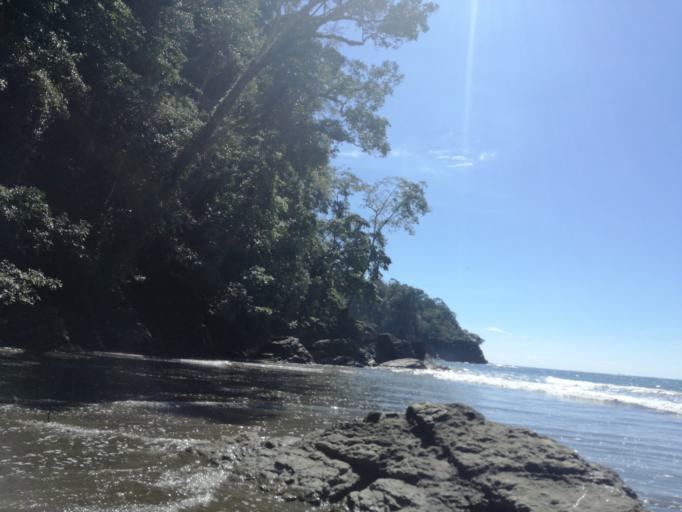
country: CR
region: San Jose
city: Mercedes
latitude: 9.0894
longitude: -83.6768
